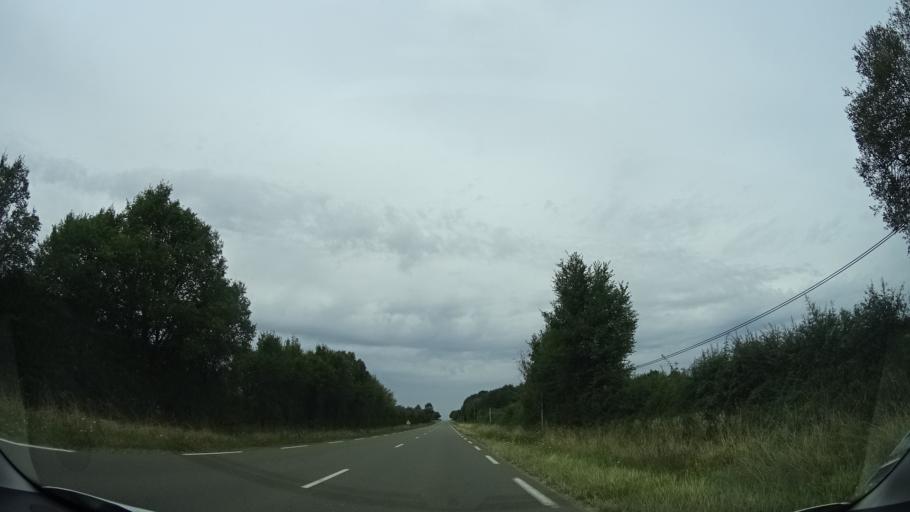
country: FR
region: Pays de la Loire
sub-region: Departement de la Mayenne
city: Meslay-du-Maine
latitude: 47.9910
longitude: -0.6285
